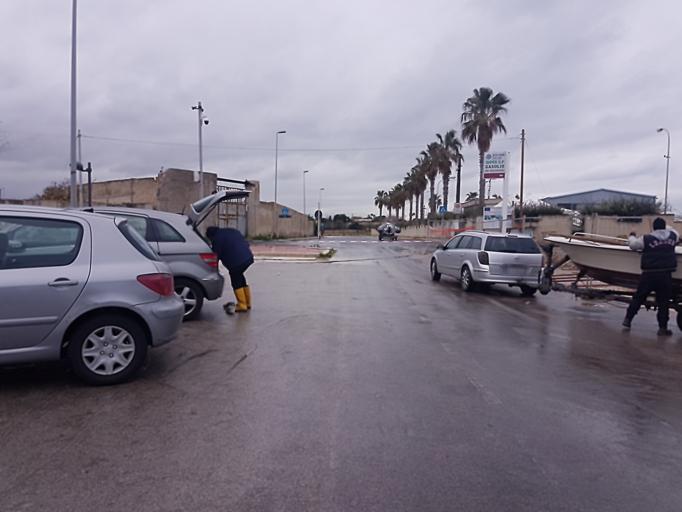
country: IT
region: Apulia
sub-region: Provincia di Bari
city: San Paolo
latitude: 41.1400
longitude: 16.8098
